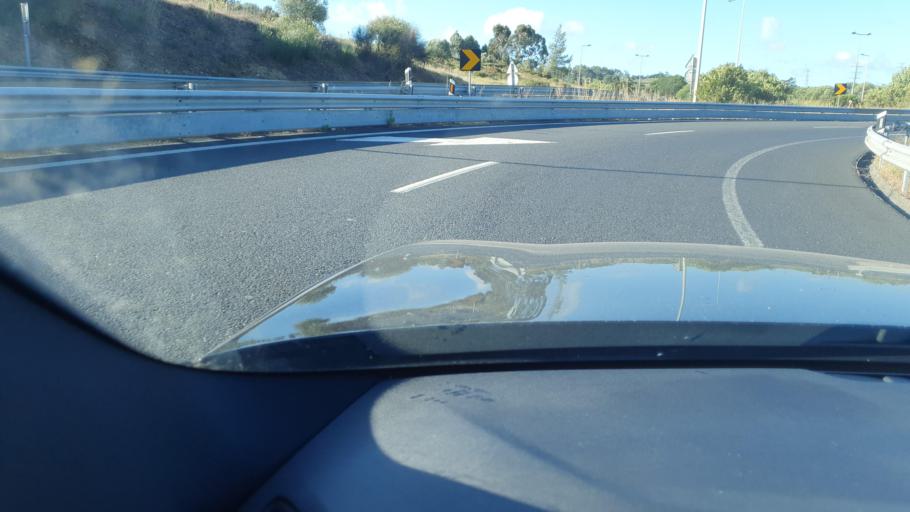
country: PT
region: Lisbon
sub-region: Odivelas
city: Canecas
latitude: 38.7920
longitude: -9.2377
